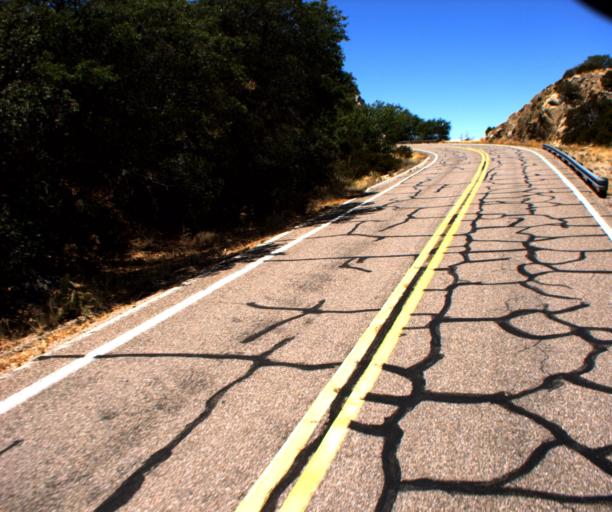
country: US
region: Arizona
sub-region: Pima County
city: Sells
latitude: 31.9728
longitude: -111.6169
